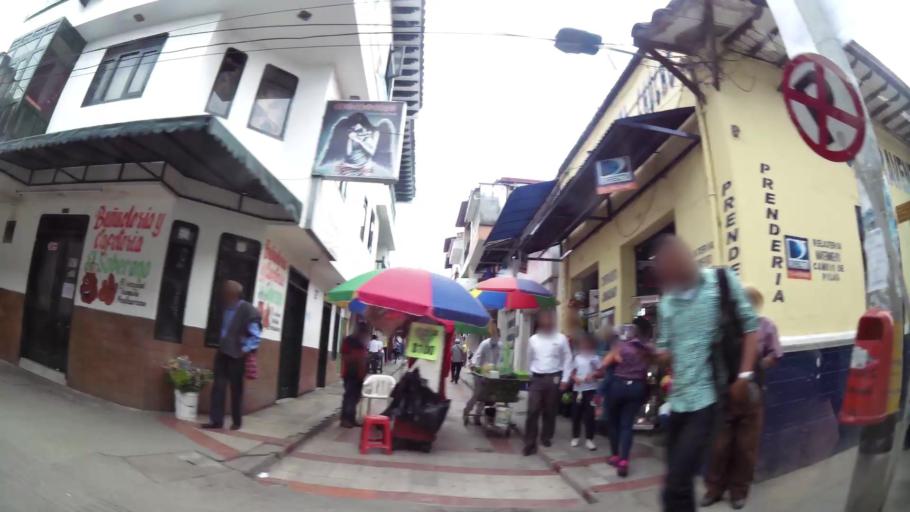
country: CO
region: Antioquia
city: Rionegro
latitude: 6.1545
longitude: -75.3734
